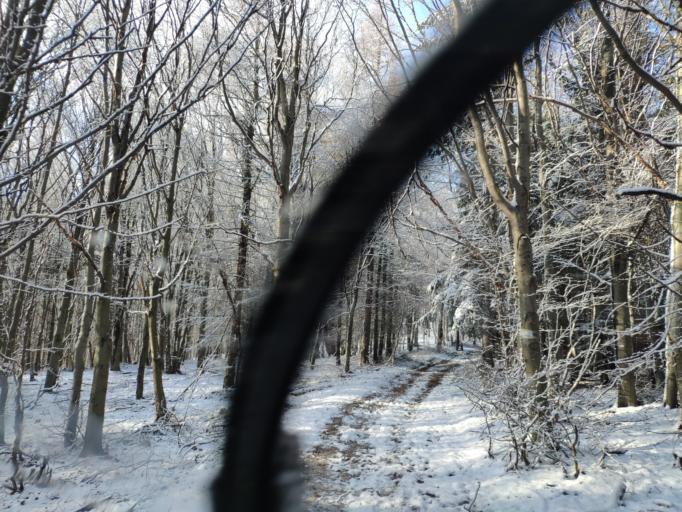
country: SK
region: Kosicky
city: Moldava nad Bodvou
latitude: 48.7427
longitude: 21.0884
